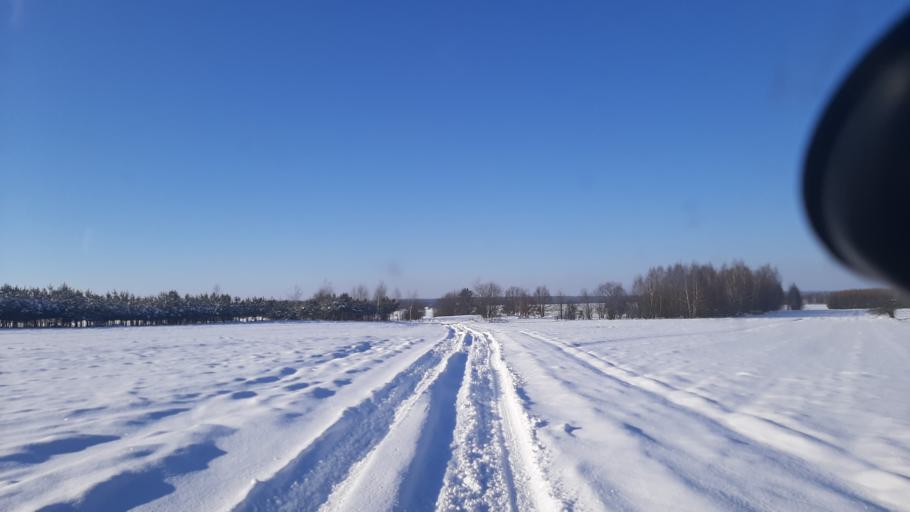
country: PL
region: Lublin Voivodeship
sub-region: Powiat lubelski
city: Jastkow
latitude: 51.3771
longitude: 22.4370
